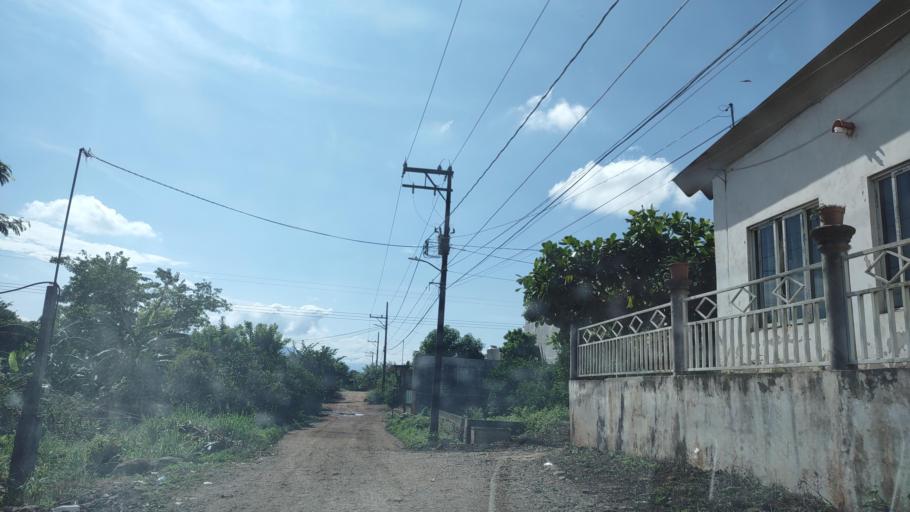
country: MX
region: Veracruz
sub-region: Martinez de la Torre
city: La Union Paso Largo
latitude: 20.1277
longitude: -96.9931
